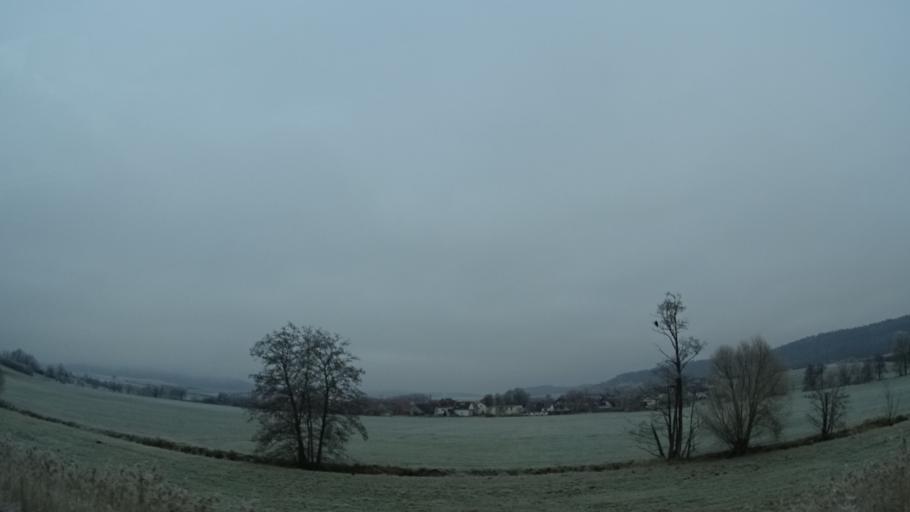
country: DE
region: Bavaria
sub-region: Regierungsbezirk Unterfranken
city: Burgpreppach
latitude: 50.1487
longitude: 10.6646
